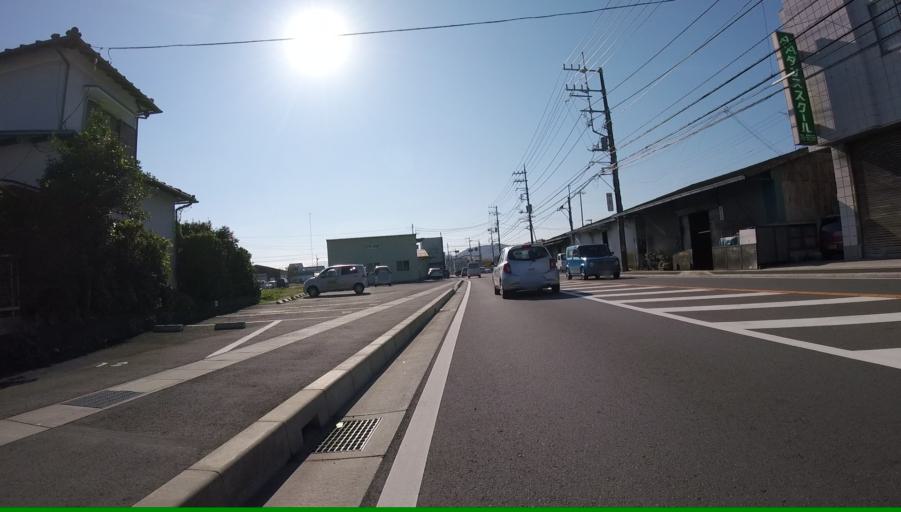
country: JP
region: Shizuoka
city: Mishima
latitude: 35.0994
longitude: 138.9153
